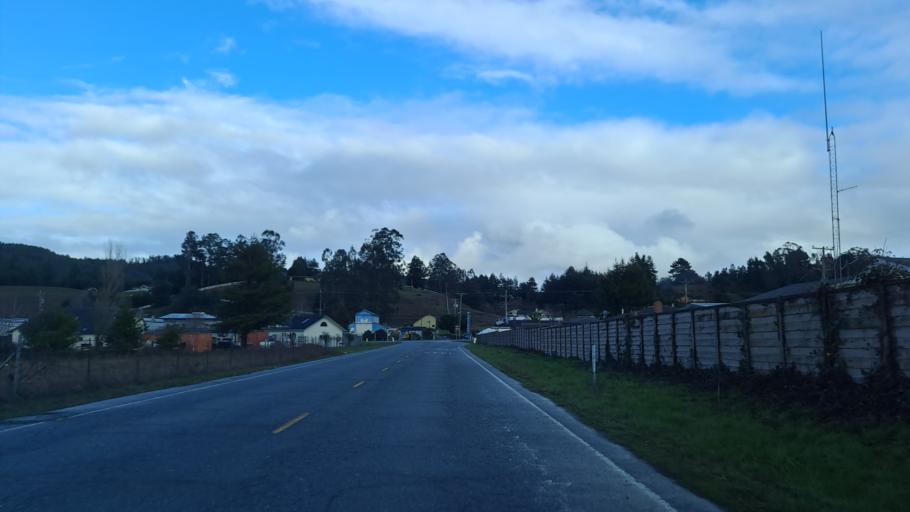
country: US
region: California
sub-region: Humboldt County
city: Fortuna
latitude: 40.5831
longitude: -124.1329
